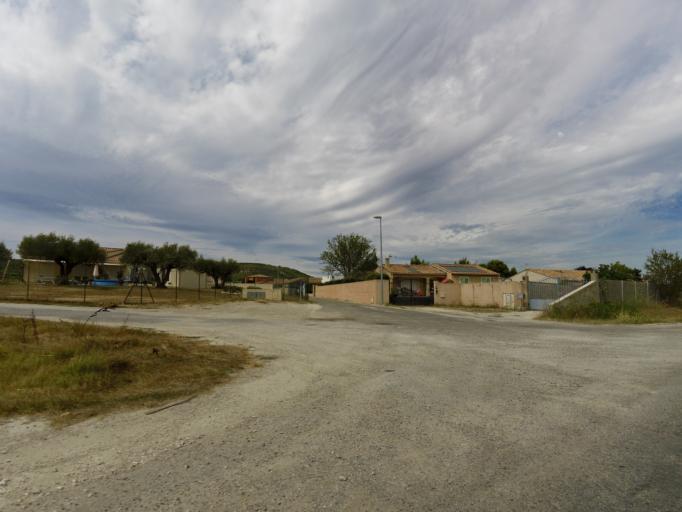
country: FR
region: Languedoc-Roussillon
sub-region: Departement du Gard
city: Calvisson
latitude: 43.7882
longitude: 4.1839
